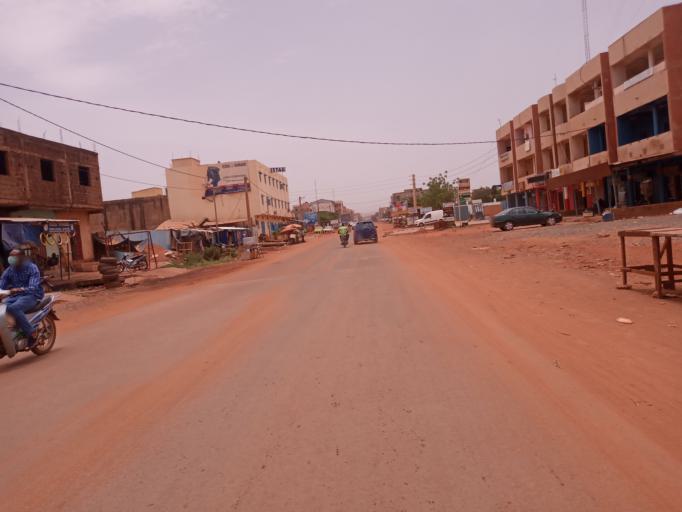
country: ML
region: Bamako
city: Bamako
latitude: 12.5824
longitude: -8.0214
